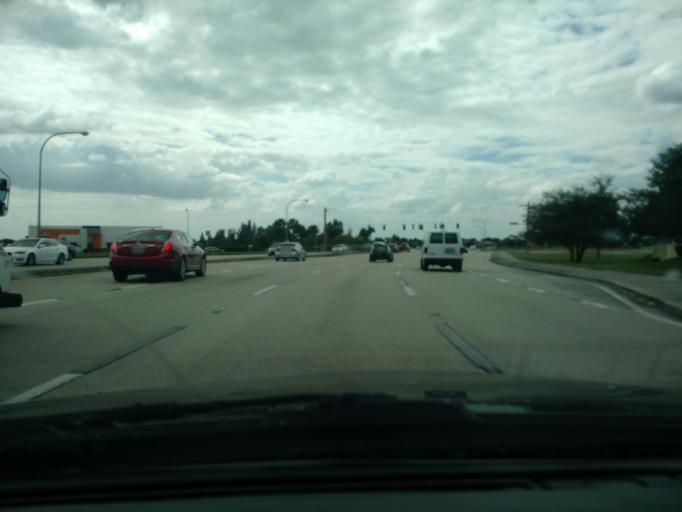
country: US
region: Florida
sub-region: Lee County
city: Pine Manor
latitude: 26.5937
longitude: -81.8652
